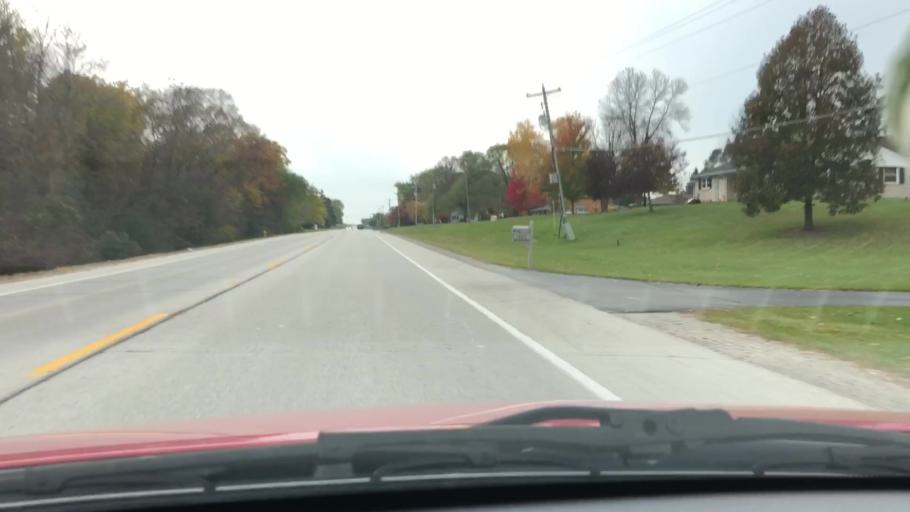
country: US
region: Wisconsin
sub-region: Brown County
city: De Pere
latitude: 44.4452
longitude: -88.1005
